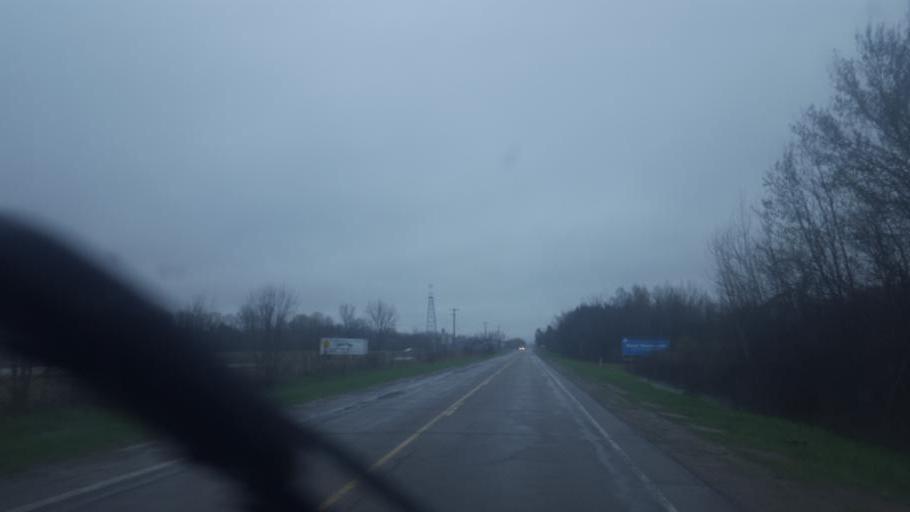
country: US
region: Michigan
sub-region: Isabella County
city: Mount Pleasant
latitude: 43.6366
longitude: -84.7682
